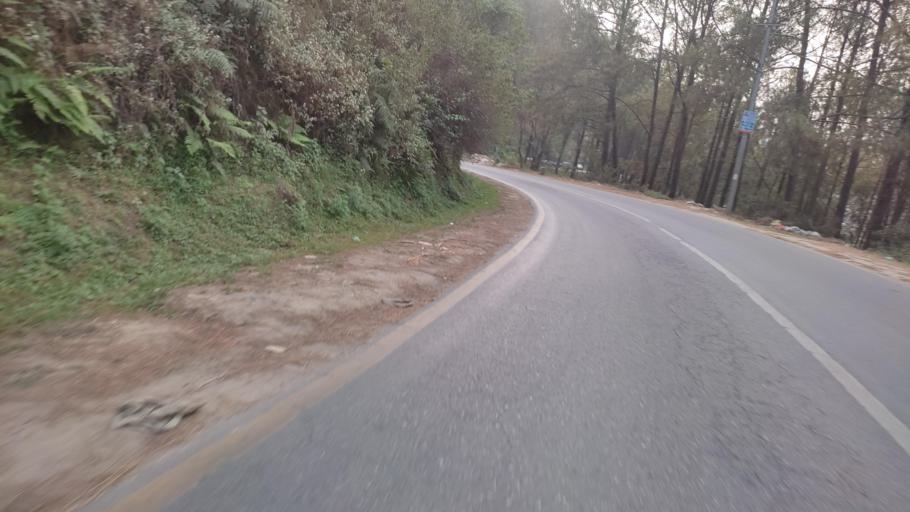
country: NP
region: Central Region
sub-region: Bagmati Zone
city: Patan
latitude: 27.6678
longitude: 85.2943
